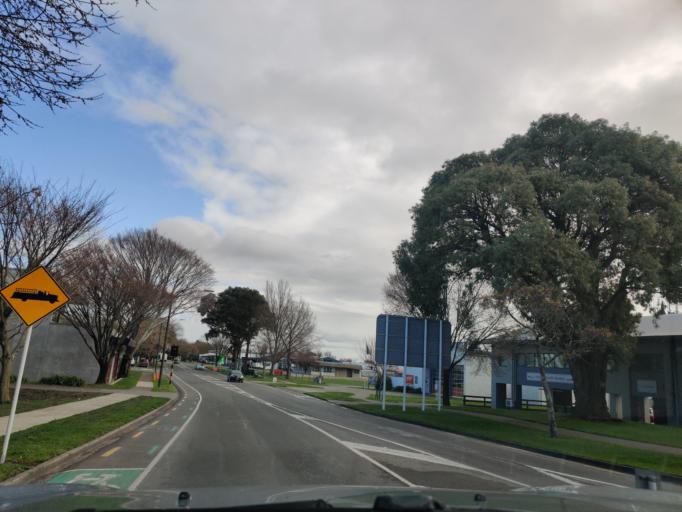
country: NZ
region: Hawke's Bay
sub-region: Hastings District
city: Hastings
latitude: -39.6676
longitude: 176.8795
